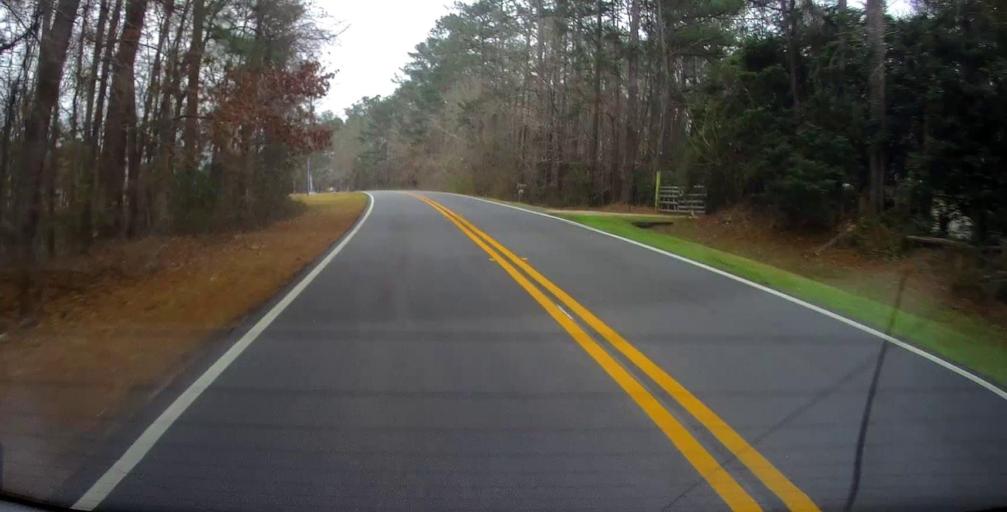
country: US
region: Georgia
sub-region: Bibb County
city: Macon
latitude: 32.9098
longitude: -83.7144
